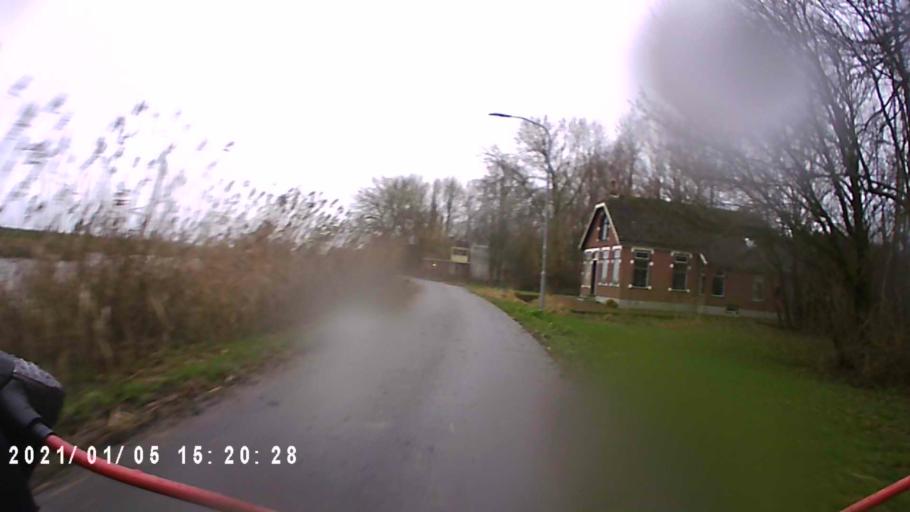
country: DE
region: Lower Saxony
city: Bunde
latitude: 53.2303
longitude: 7.2077
